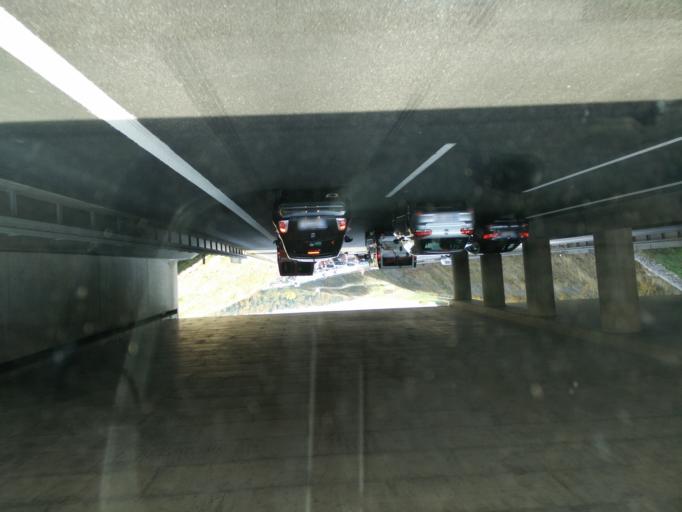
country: DE
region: Baden-Wuerttemberg
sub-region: Karlsruhe Region
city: Konigsbach-Stein
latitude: 48.9376
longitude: 8.5319
